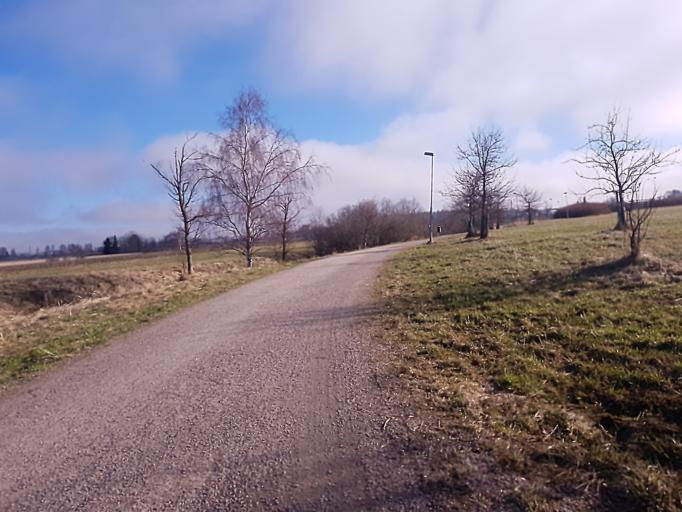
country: FI
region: Uusimaa
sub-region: Helsinki
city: Helsinki
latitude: 60.2650
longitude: 24.9487
